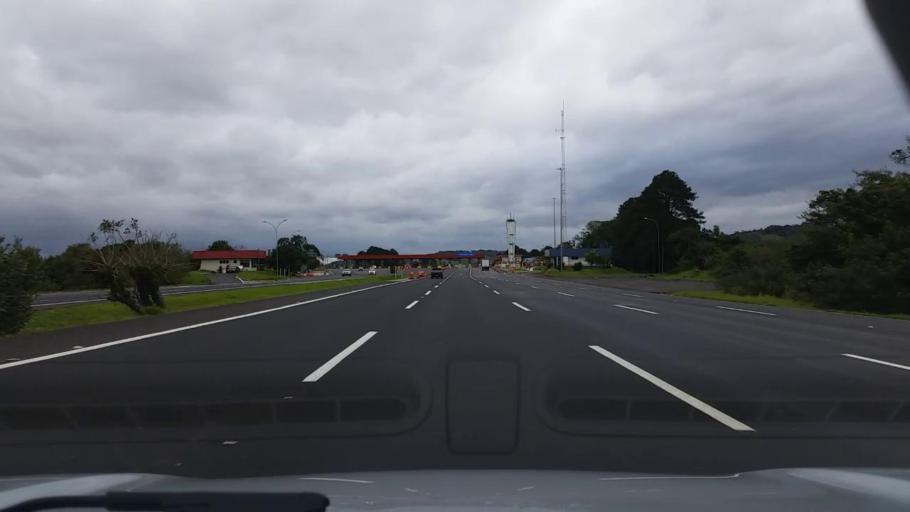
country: BR
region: Rio Grande do Sul
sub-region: Osorio
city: Osorio
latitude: -29.8842
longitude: -50.4446
